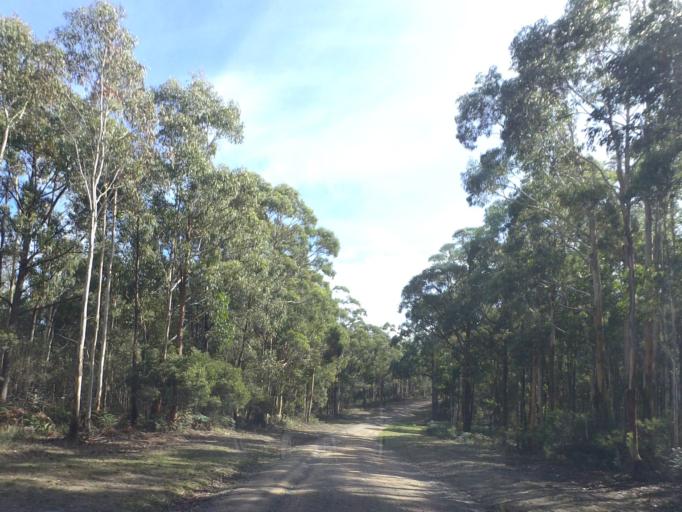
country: AU
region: Victoria
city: Brown Hill
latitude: -37.4421
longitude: 144.2058
